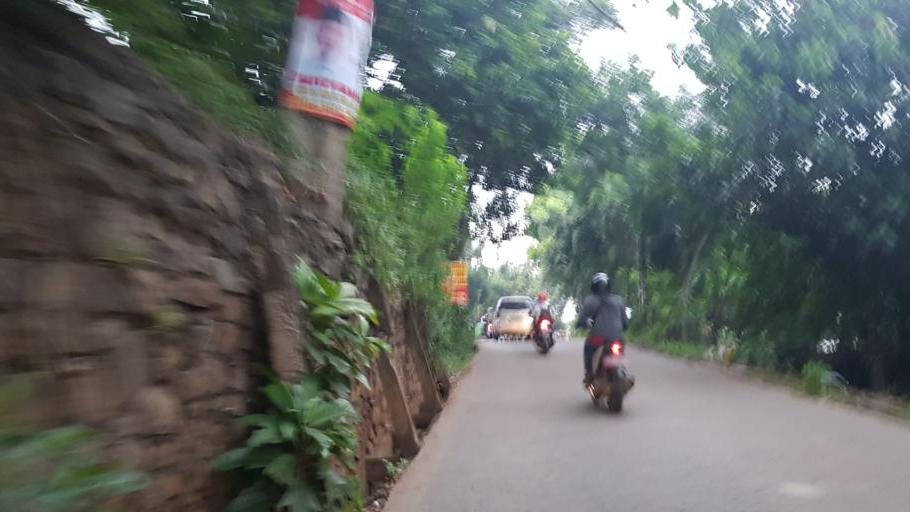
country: ID
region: West Java
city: Sawangan
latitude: -6.3653
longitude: 106.7935
